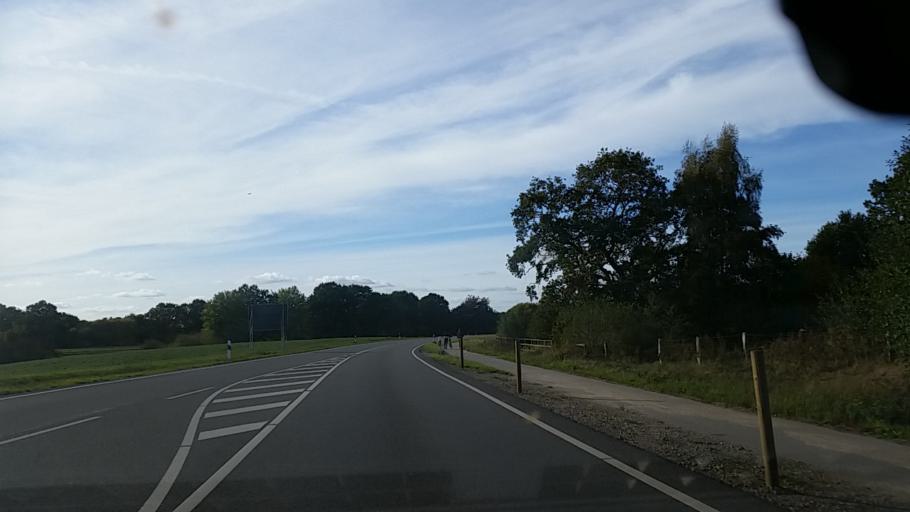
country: DE
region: Schleswig-Holstein
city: Bargteheide
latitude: 53.7205
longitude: 10.2504
